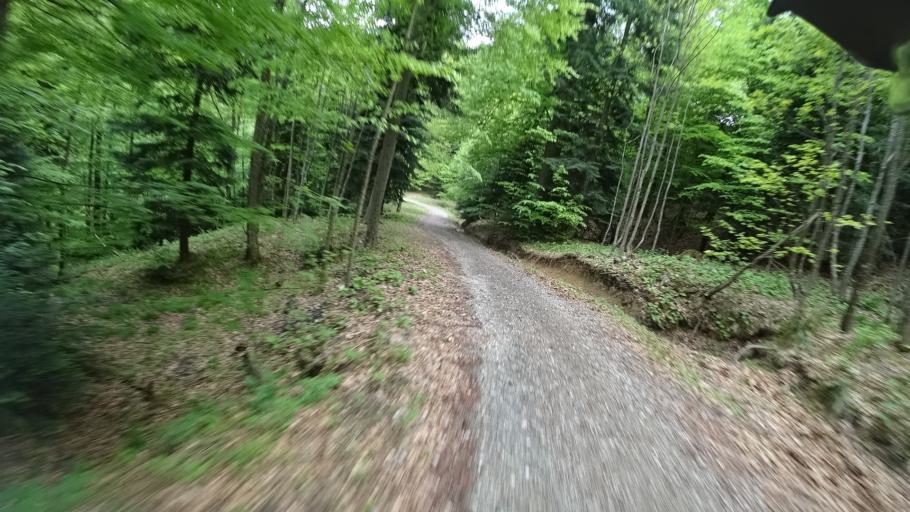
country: HR
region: Grad Zagreb
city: Kasina
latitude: 45.9146
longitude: 15.9398
